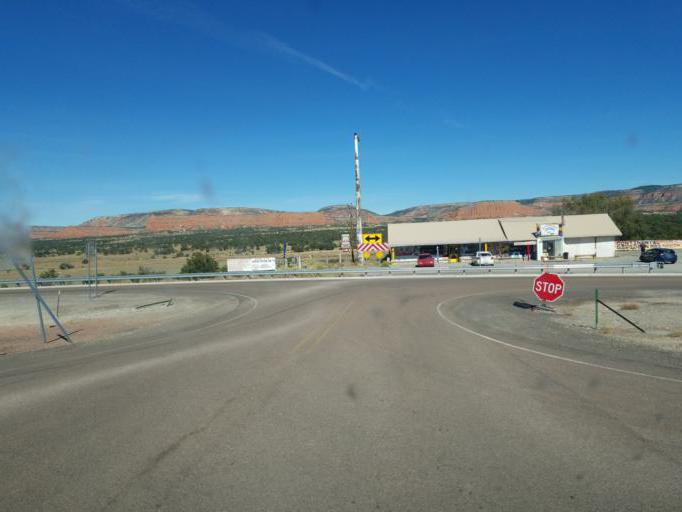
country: US
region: New Mexico
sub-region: McKinley County
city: Thoreau
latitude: 35.4240
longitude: -108.3120
